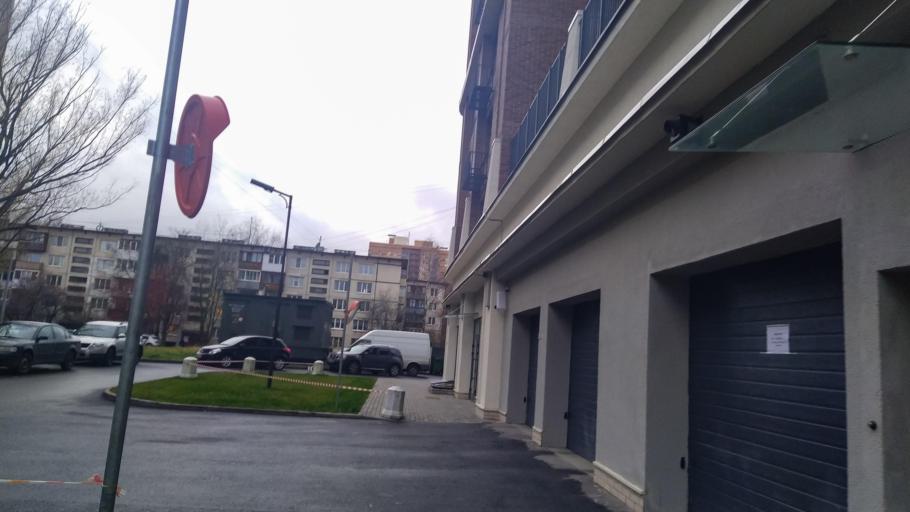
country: RU
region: St.-Petersburg
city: Grazhdanka
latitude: 60.0283
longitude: 30.4155
